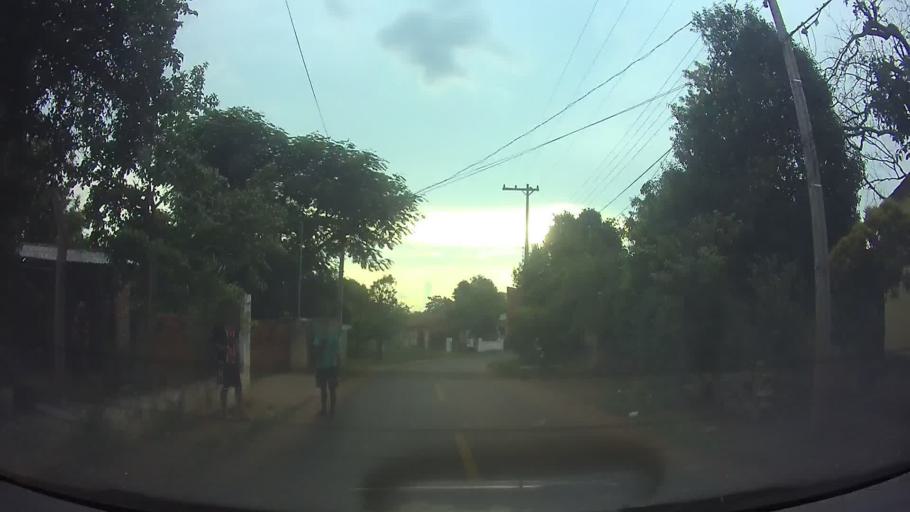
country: PY
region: Central
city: San Lorenzo
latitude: -25.2792
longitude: -57.4792
